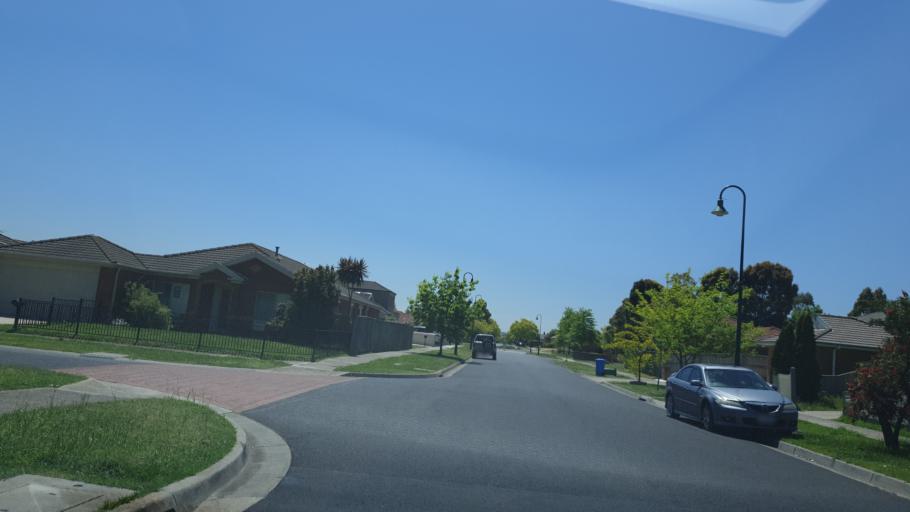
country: AU
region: Victoria
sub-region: Casey
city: Cranbourne North
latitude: -38.0663
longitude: 145.2831
